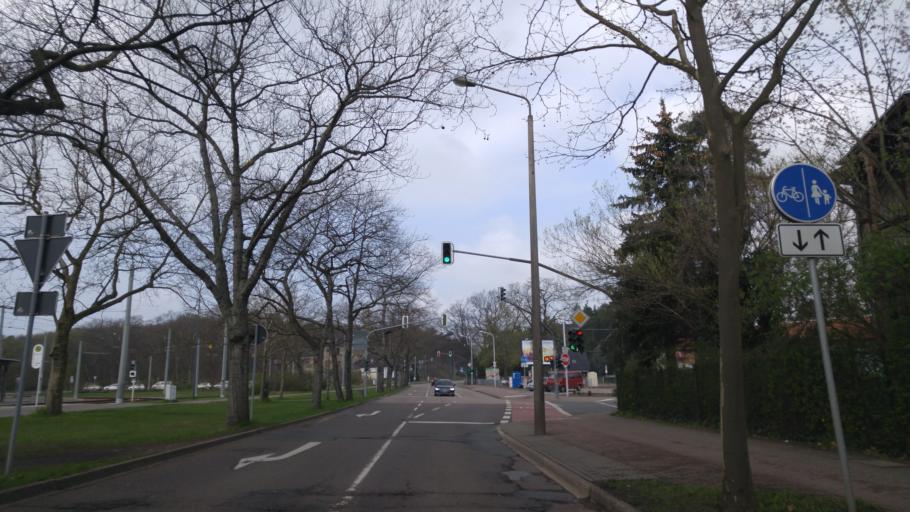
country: DE
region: Saxony-Anhalt
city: Halle Neustadt
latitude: 51.5001
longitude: 11.9335
